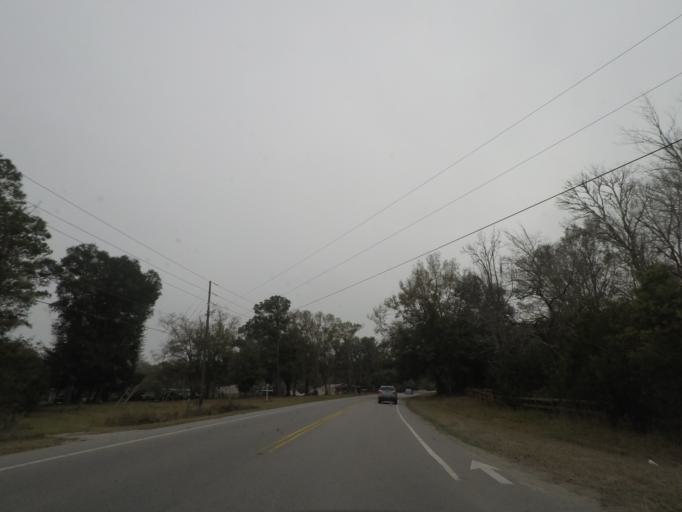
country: US
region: South Carolina
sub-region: Charleston County
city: Seabrook Island
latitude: 32.5308
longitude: -80.2953
